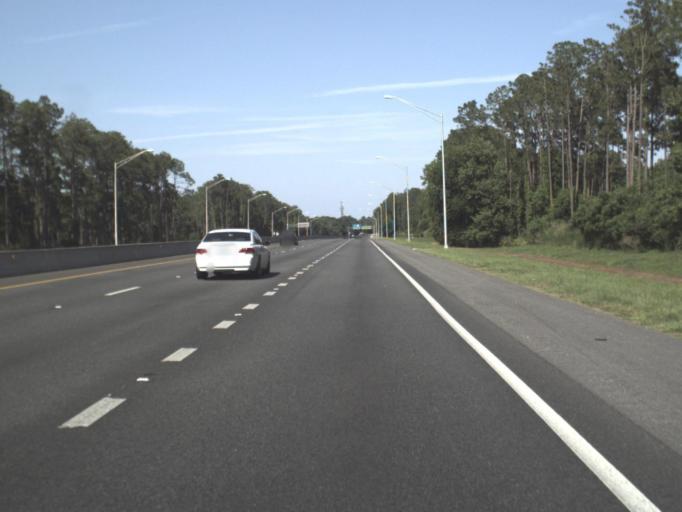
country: US
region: Florida
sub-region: Saint Johns County
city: Ponte Vedra Beach
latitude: 30.2535
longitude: -81.4495
